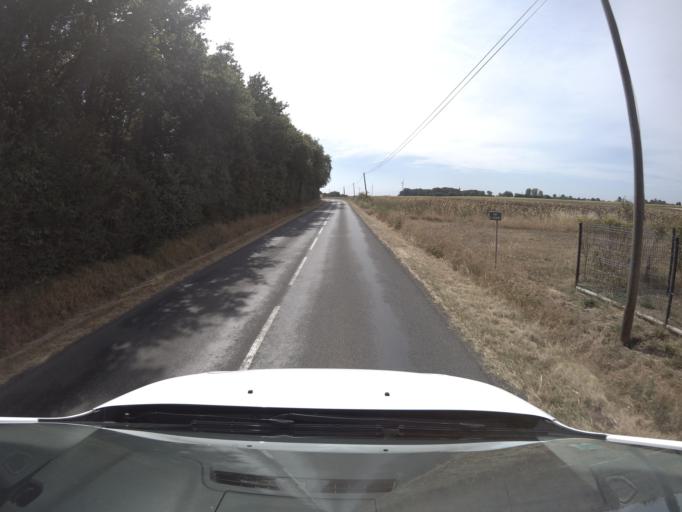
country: FR
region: Poitou-Charentes
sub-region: Departement des Deux-Sevres
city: Saint-Leger-de-Montbrun
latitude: 46.9929
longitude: -0.1333
